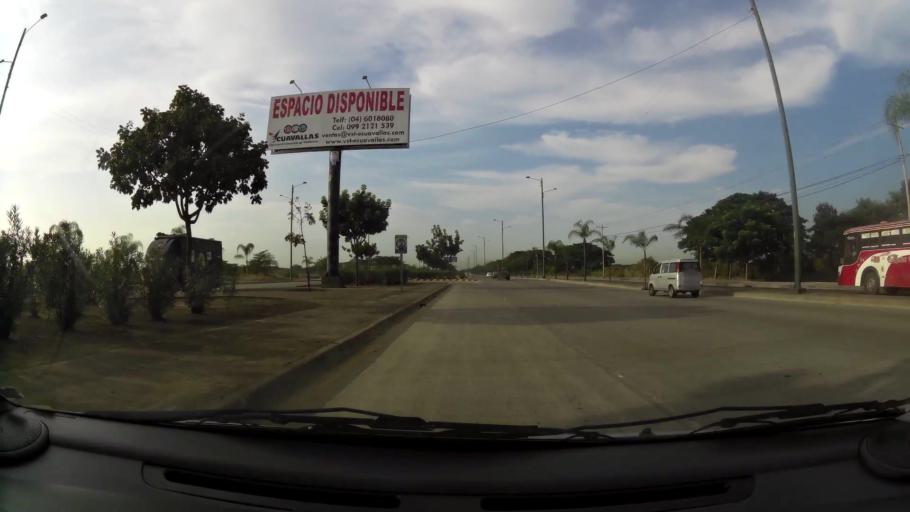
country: EC
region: Guayas
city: Eloy Alfaro
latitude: -2.0908
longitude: -79.8948
